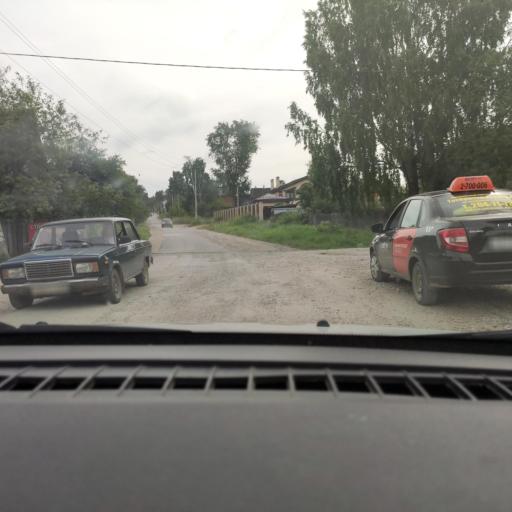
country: RU
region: Perm
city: Kondratovo
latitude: 58.0500
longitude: 56.0471
